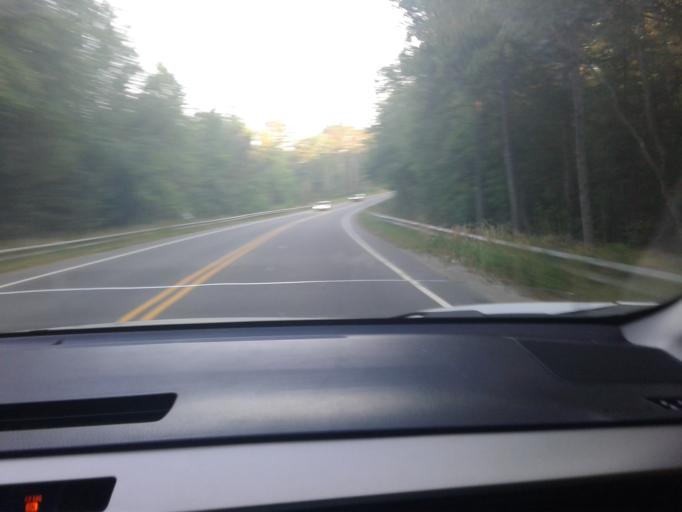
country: US
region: North Carolina
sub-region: Harnett County
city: Lillington
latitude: 35.4285
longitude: -78.8241
